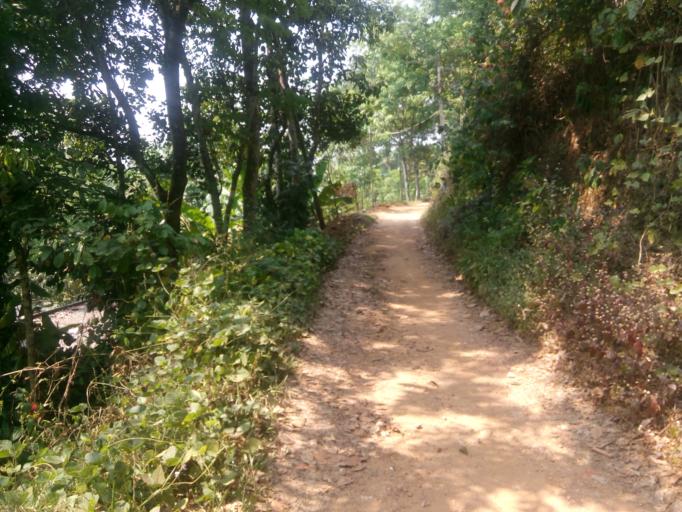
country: IN
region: Kerala
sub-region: Kottayam
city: Erattupetta
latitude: 9.5511
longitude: 76.7364
